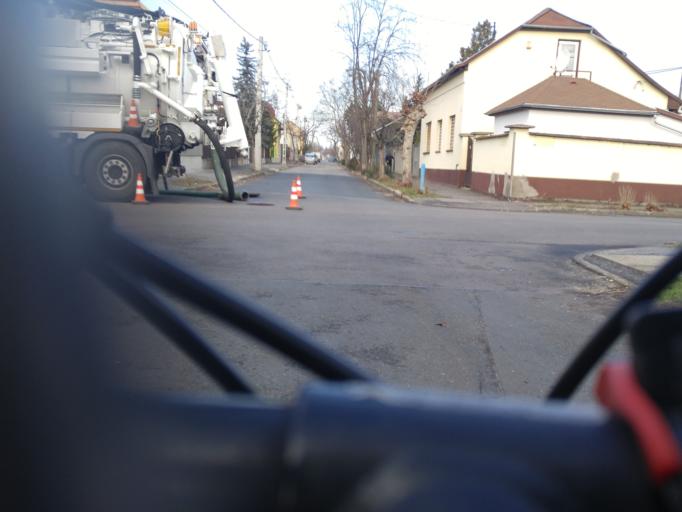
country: HU
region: Budapest
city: Budapest XX. keruelet
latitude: 47.4343
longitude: 19.1205
